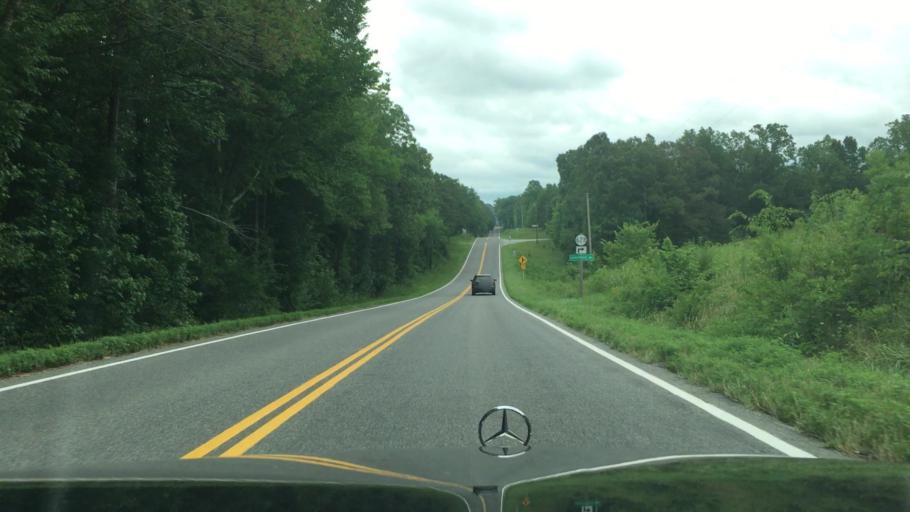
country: US
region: Virginia
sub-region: Nottoway County
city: Crewe
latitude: 37.2801
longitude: -78.1931
